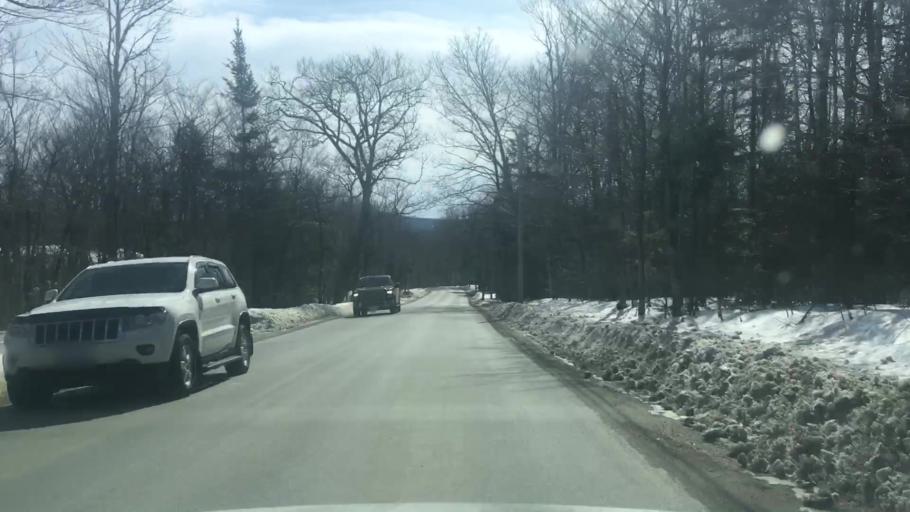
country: US
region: Maine
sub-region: Penobscot County
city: Holden
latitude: 44.7615
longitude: -68.6419
